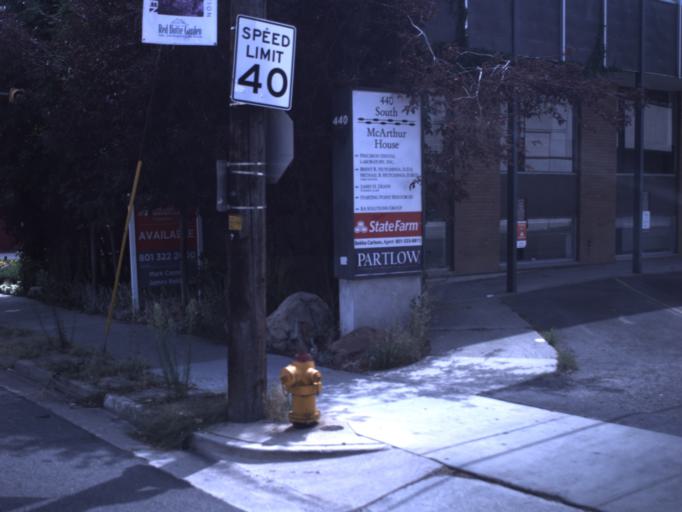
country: US
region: Utah
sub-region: Salt Lake County
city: Salt Lake City
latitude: 40.7596
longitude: -111.8712
